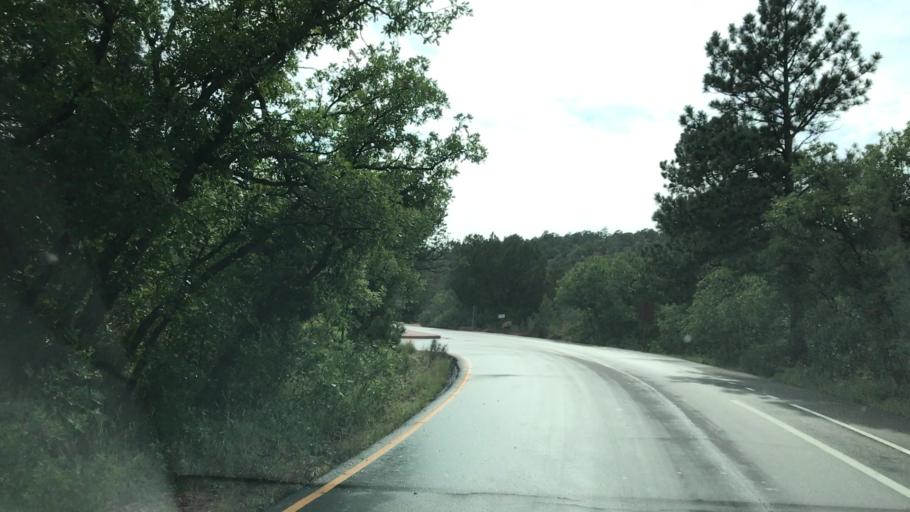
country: US
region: Colorado
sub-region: El Paso County
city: Manitou Springs
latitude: 38.8662
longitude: -104.8956
